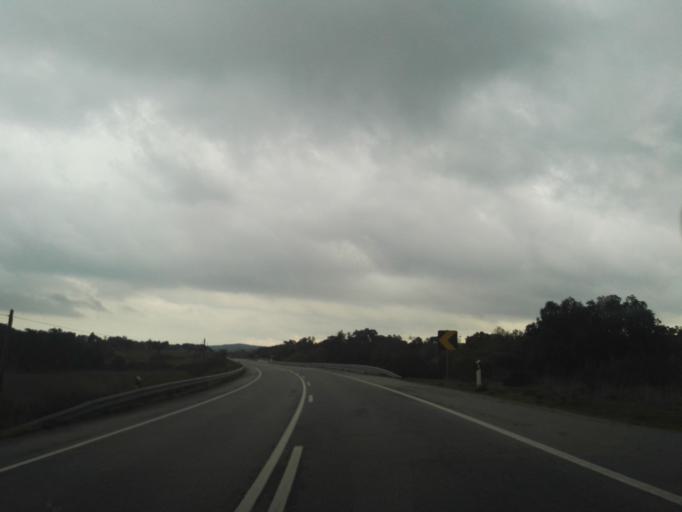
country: PT
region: Portalegre
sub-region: Portalegre
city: Urra
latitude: 39.1975
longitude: -7.3645
